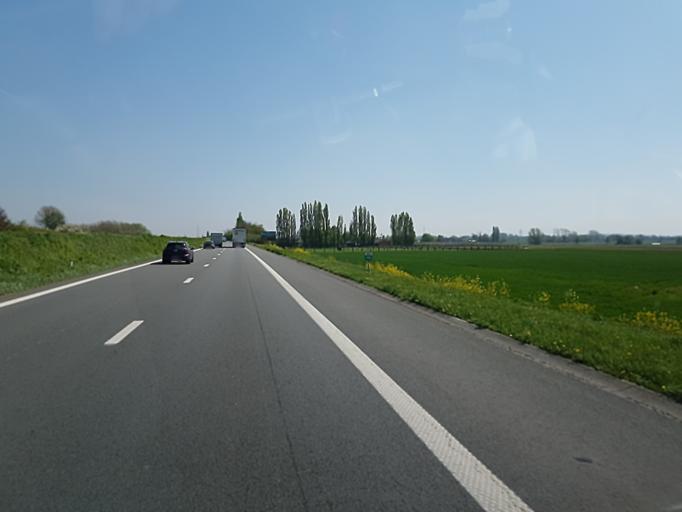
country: BE
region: Flanders
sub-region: Provincie West-Vlaanderen
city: Menen
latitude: 50.8188
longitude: 3.0844
